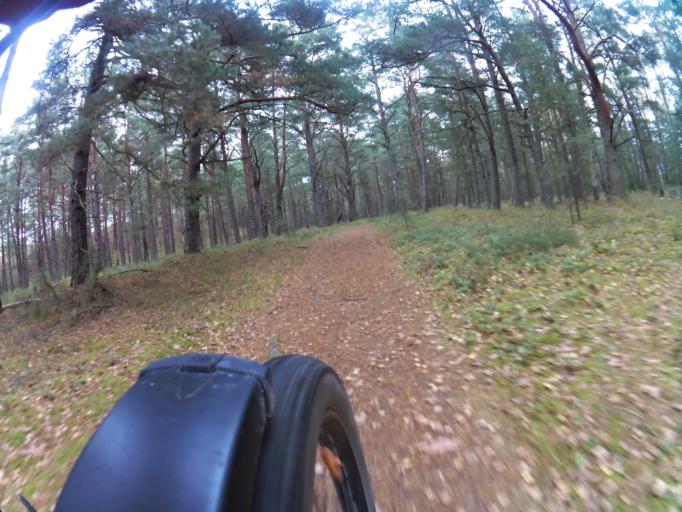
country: PL
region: Pomeranian Voivodeship
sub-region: Powiat leborski
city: Leba
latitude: 54.7714
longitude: 17.6332
